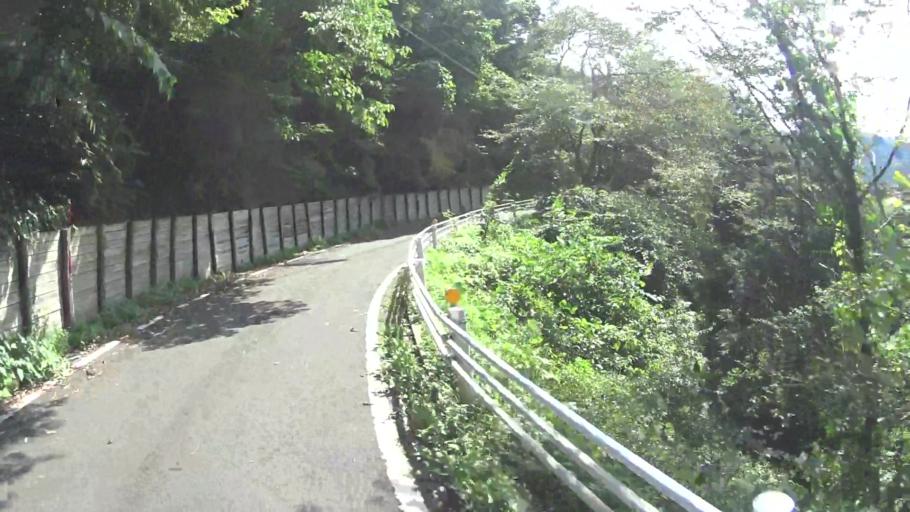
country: JP
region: Kyoto
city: Miyazu
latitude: 35.6827
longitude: 135.2349
